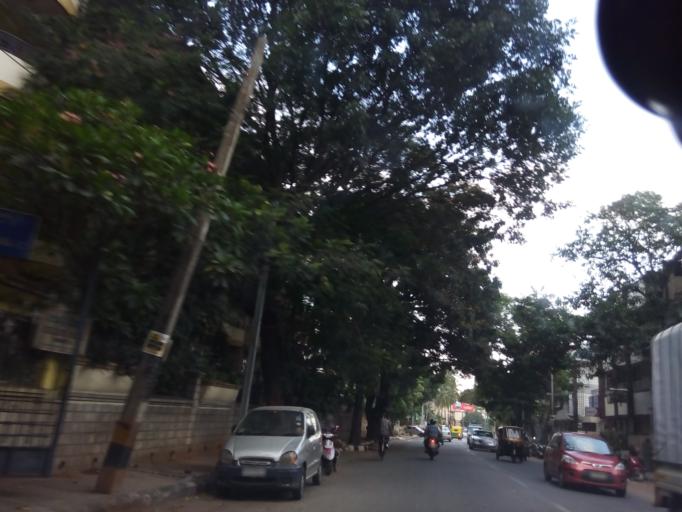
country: IN
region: Karnataka
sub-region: Bangalore Urban
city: Bangalore
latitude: 13.0029
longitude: 77.5971
